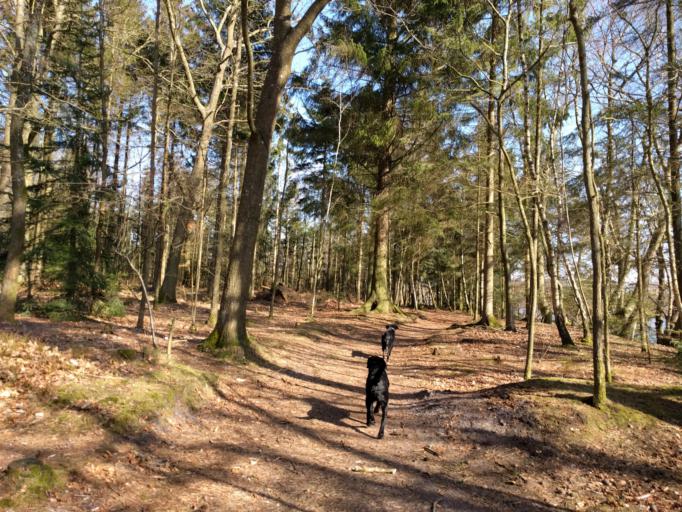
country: DK
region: Central Jutland
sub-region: Silkeborg Kommune
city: Silkeborg
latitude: 56.1696
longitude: 9.5313
